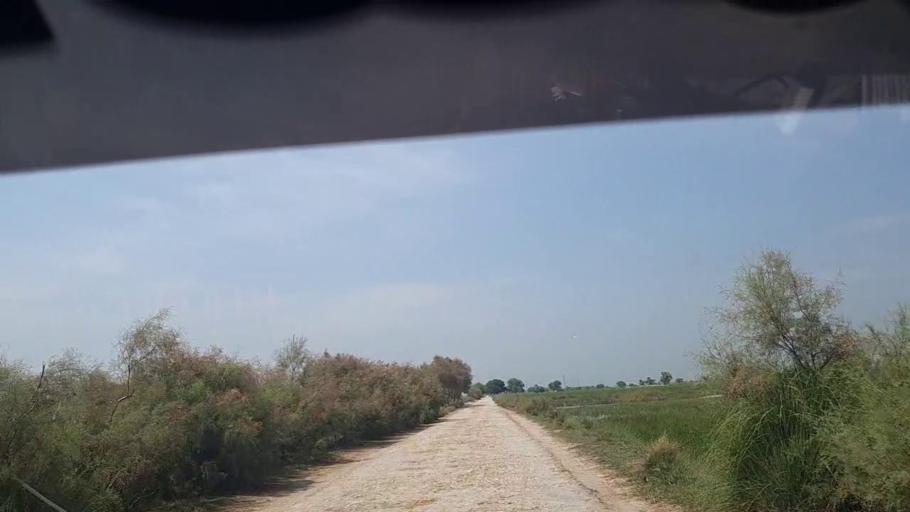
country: PK
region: Sindh
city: Thul
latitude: 28.1718
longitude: 68.7509
